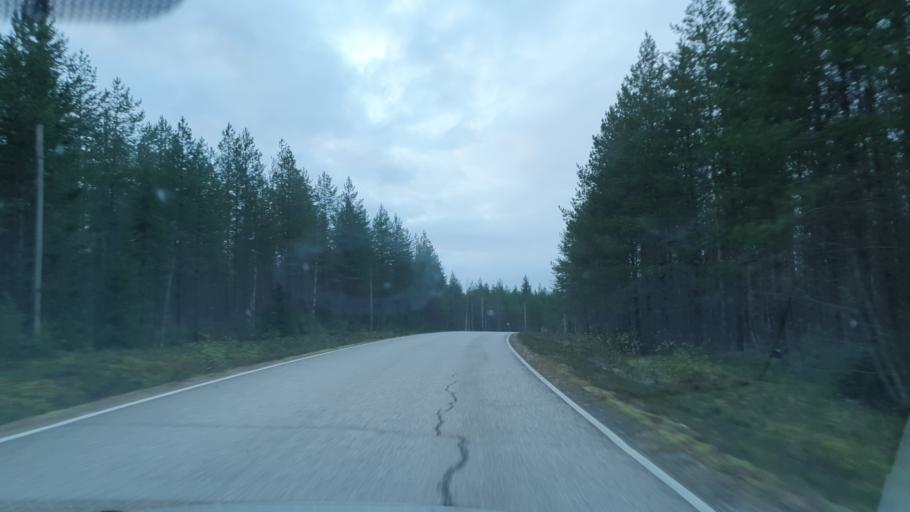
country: FI
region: Kainuu
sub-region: Kajaani
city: Ristijaervi
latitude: 64.4304
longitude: 28.3715
